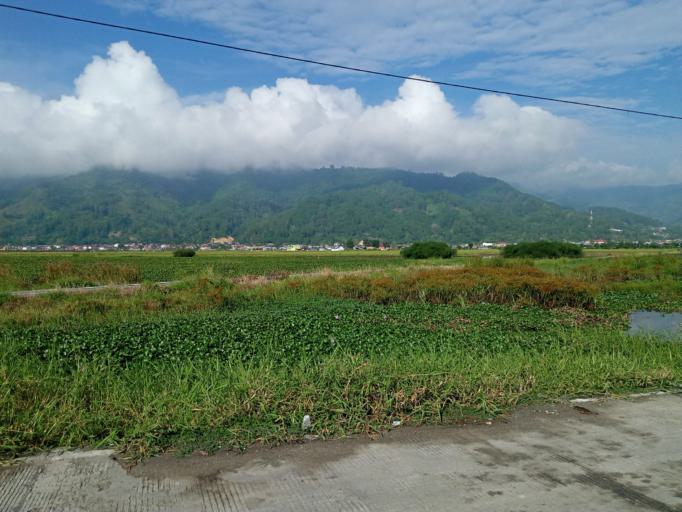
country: ID
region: Jambi
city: Sungai Penuh
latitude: -2.0696
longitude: 101.4178
